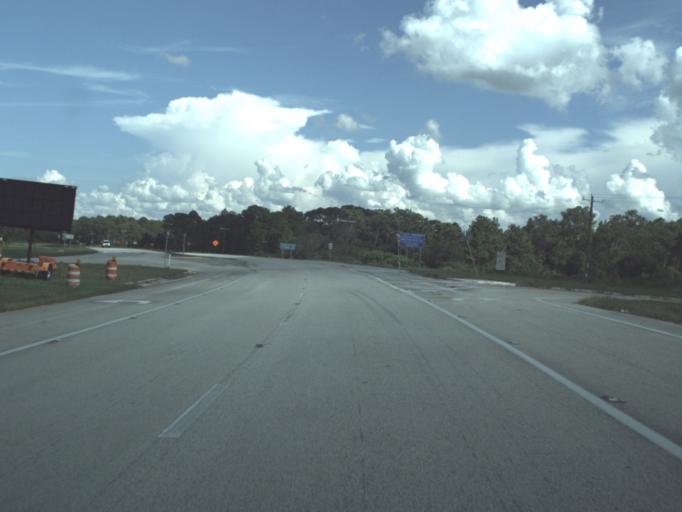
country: US
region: Florida
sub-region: Polk County
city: Babson Park
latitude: 27.8064
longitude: -81.3167
